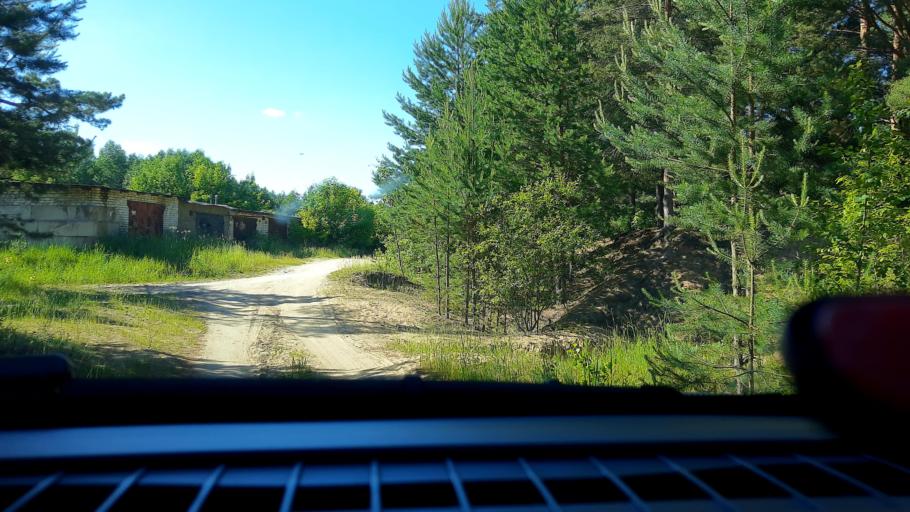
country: RU
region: Nizjnij Novgorod
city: Gidrotorf
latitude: 56.5049
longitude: 43.5386
